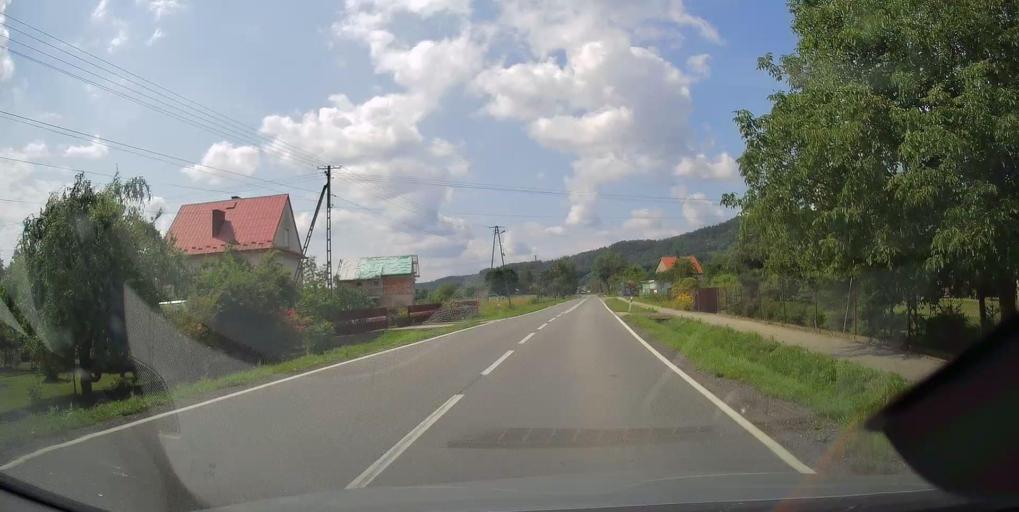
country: PL
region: Lesser Poland Voivodeship
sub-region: Powiat tarnowski
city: Wielka Wies
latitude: 49.9064
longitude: 20.8180
